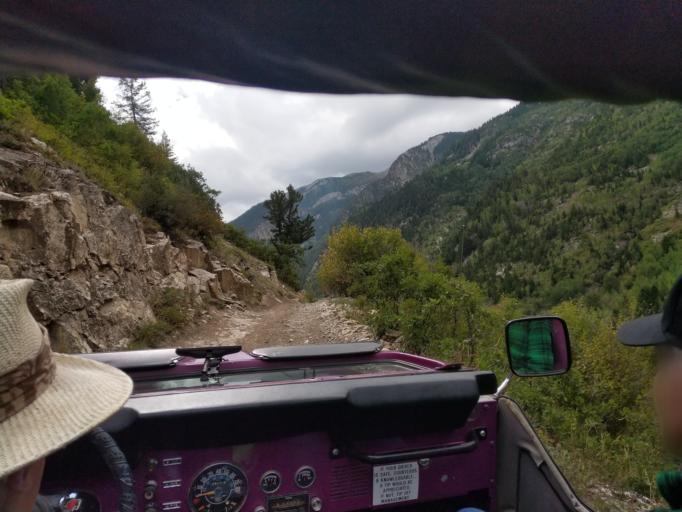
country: US
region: Colorado
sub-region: Gunnison County
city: Crested Butte
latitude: 39.0592
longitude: -107.1376
